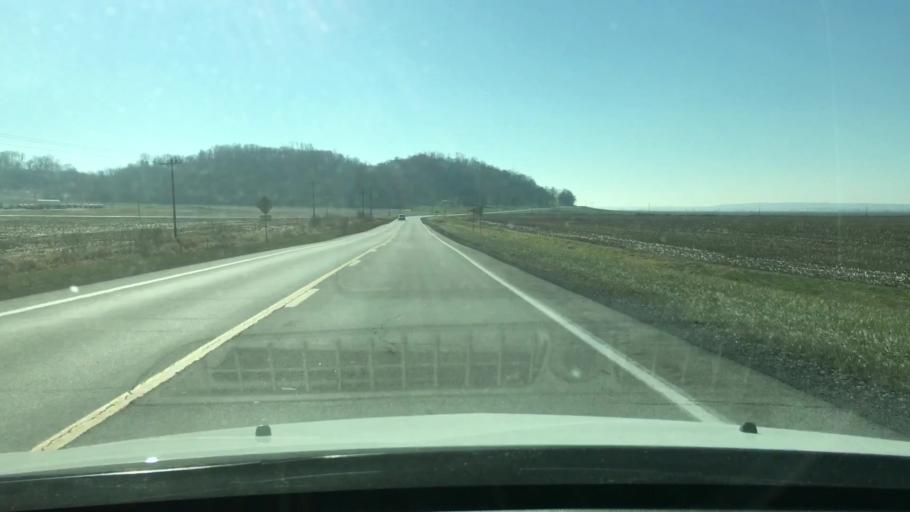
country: US
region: Illinois
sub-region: Morgan County
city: Meredosia
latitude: 39.7086
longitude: -90.5688
